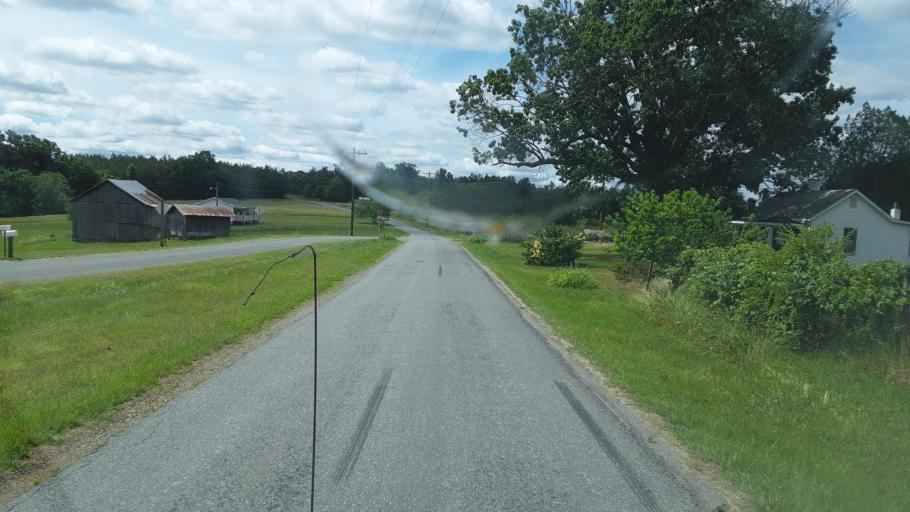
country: US
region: Virginia
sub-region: Pittsylvania County
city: Chatham
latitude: 36.8418
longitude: -79.4462
